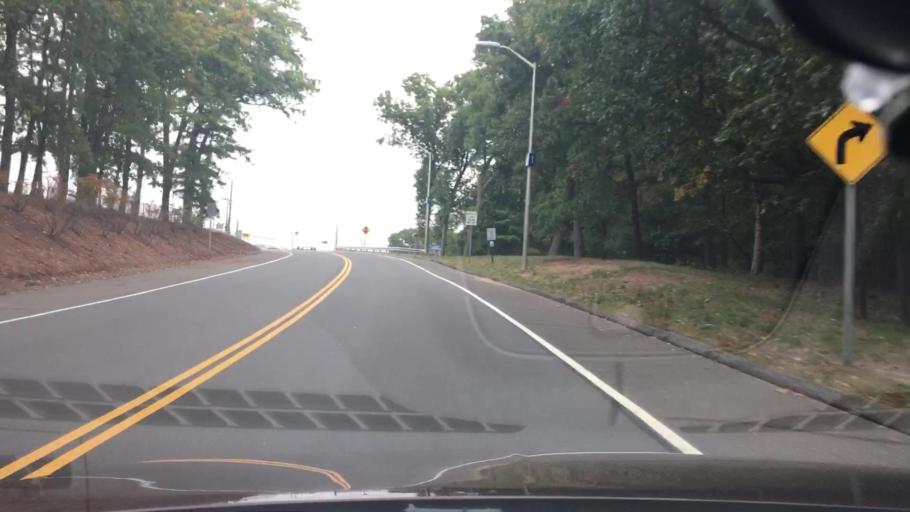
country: US
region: Connecticut
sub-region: Hartford County
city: Windsor Locks
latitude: 41.9205
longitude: -72.6844
